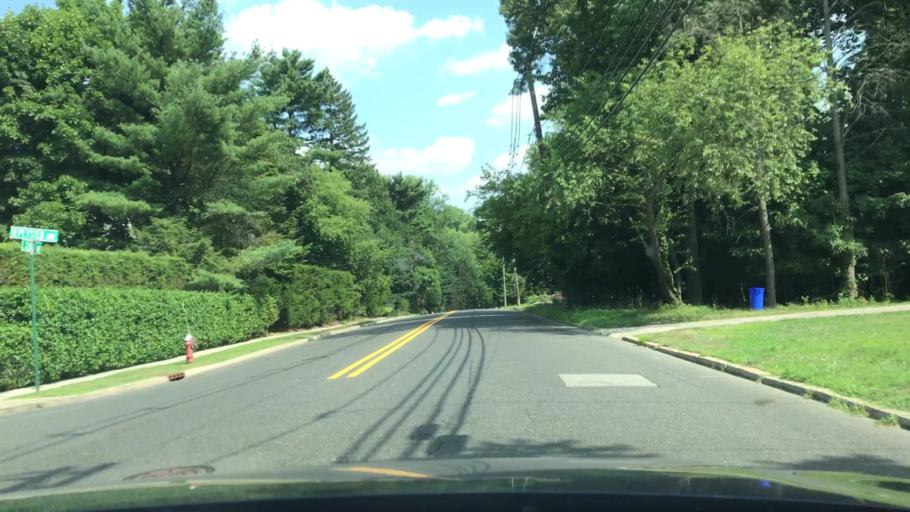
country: US
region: New Jersey
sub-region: Bergen County
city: Tenafly
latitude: 40.9193
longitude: -73.9573
